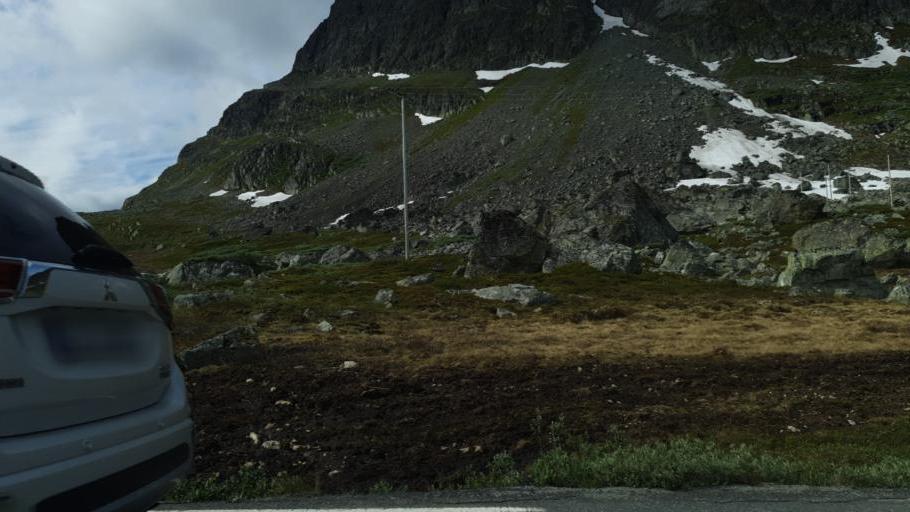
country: NO
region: Oppland
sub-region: Vestre Slidre
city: Slidre
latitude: 61.3001
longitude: 8.8094
